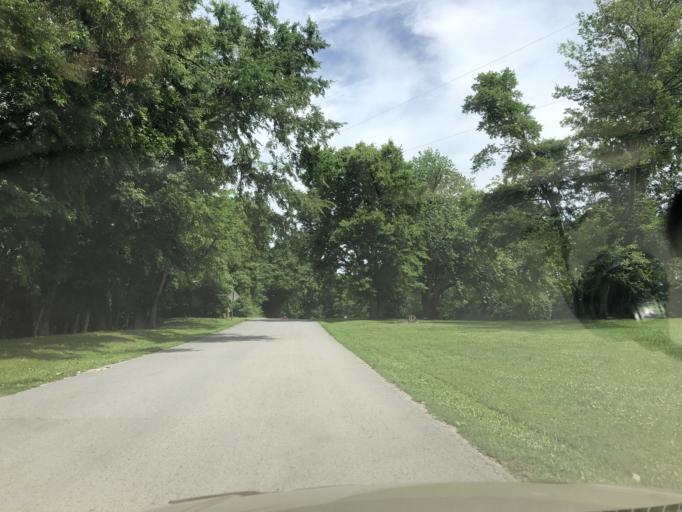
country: US
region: Tennessee
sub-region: Davidson County
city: Lakewood
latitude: 36.2542
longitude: -86.6035
